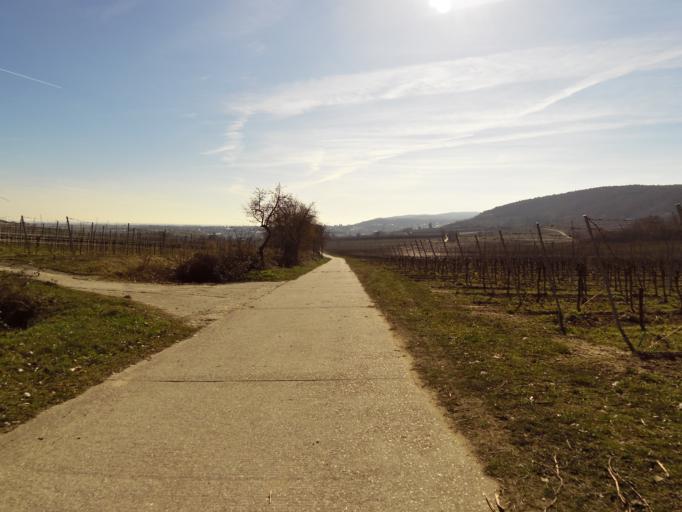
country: DE
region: Rheinland-Pfalz
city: Kallstadt
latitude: 49.4799
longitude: 8.1620
